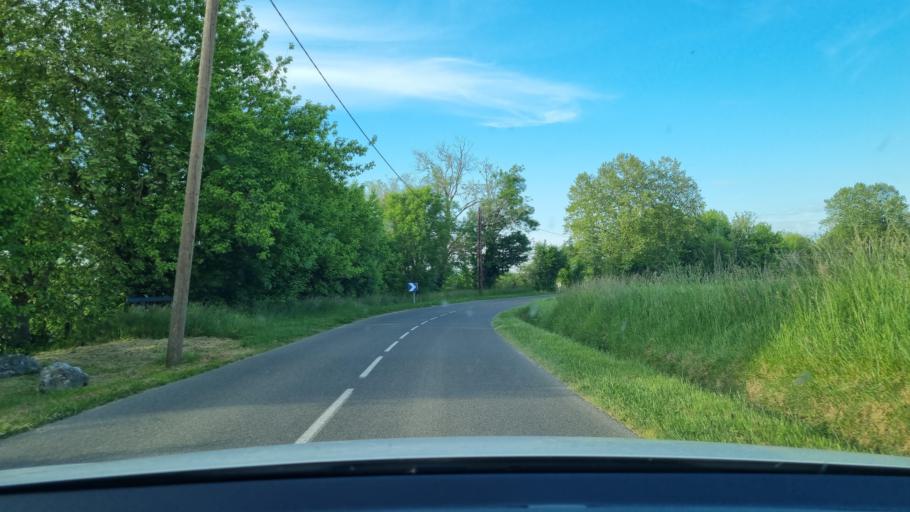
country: FR
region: Aquitaine
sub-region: Departement des Landes
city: Peyrehorade
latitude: 43.5406
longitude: -1.1419
